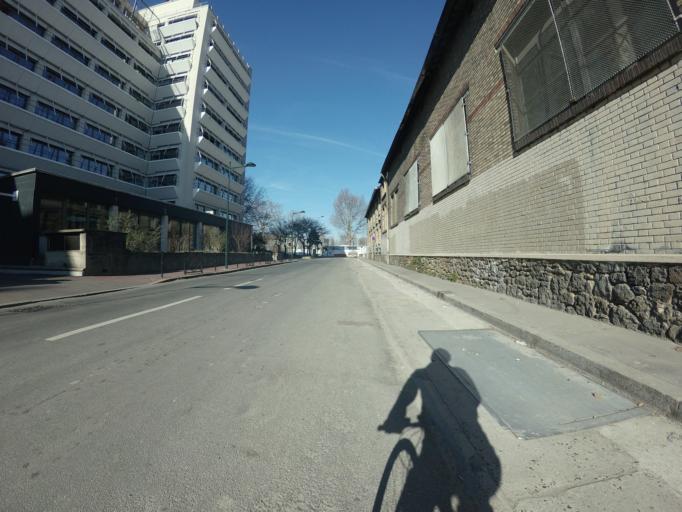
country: FR
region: Ile-de-France
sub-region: Departement des Hauts-de-Seine
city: Clichy
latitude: 48.9125
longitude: 2.3148
